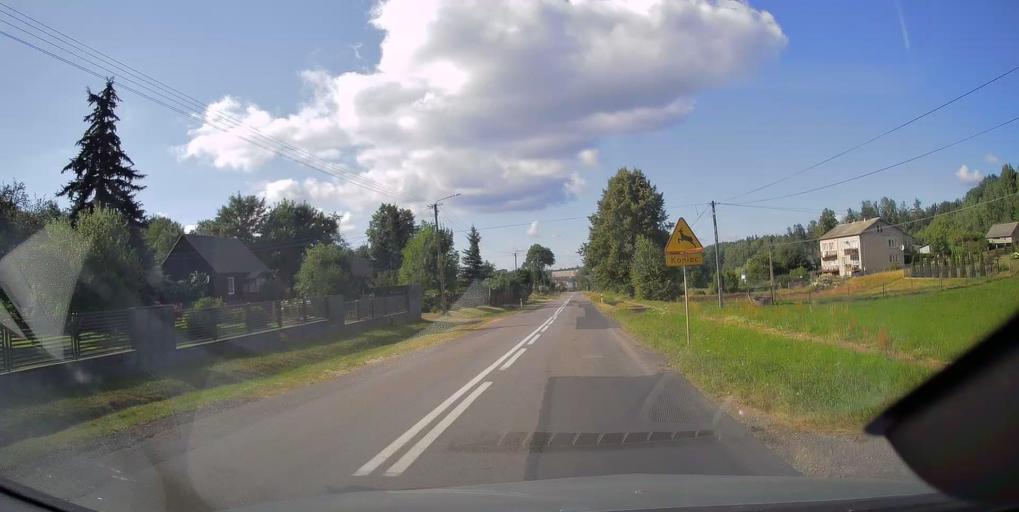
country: PL
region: Swietokrzyskie
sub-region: Powiat skarzyski
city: Suchedniow
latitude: 50.9984
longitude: 20.8513
